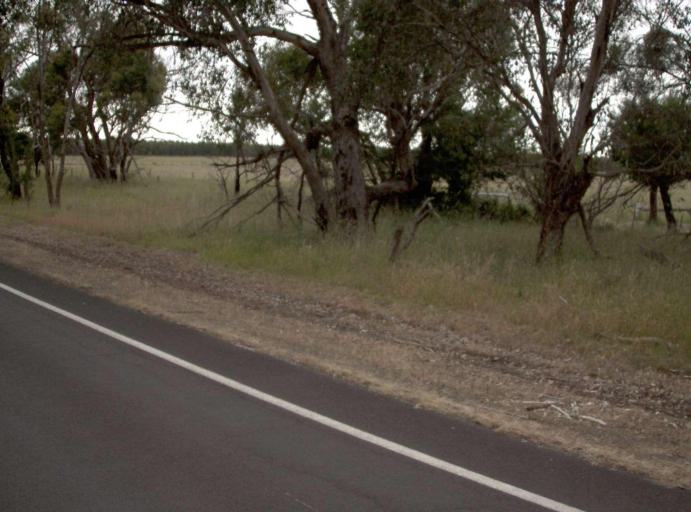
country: AU
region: Victoria
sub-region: Wellington
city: Sale
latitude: -38.4183
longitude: 146.9593
